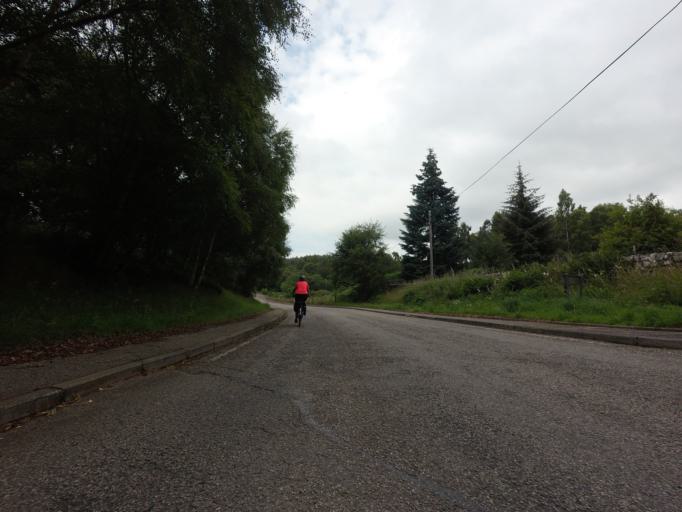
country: GB
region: Scotland
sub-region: Highland
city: Evanton
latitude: 57.9436
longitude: -4.4077
